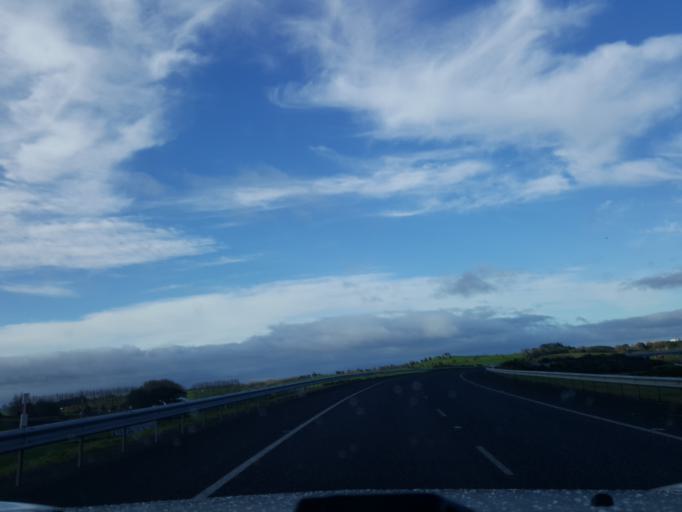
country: NZ
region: Waikato
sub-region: Waikato District
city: Ngaruawahia
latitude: -37.6813
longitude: 175.2154
